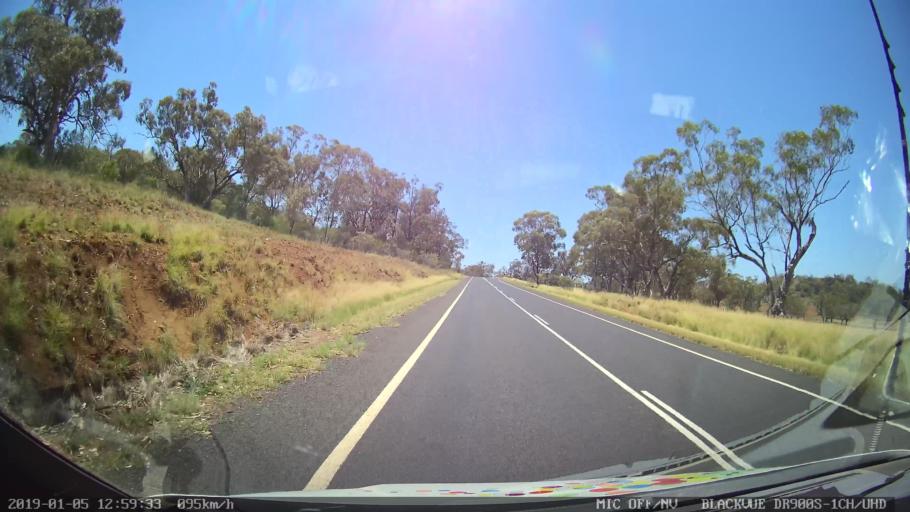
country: AU
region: New South Wales
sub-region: Narrabri
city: Boggabri
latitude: -31.1140
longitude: 149.7675
